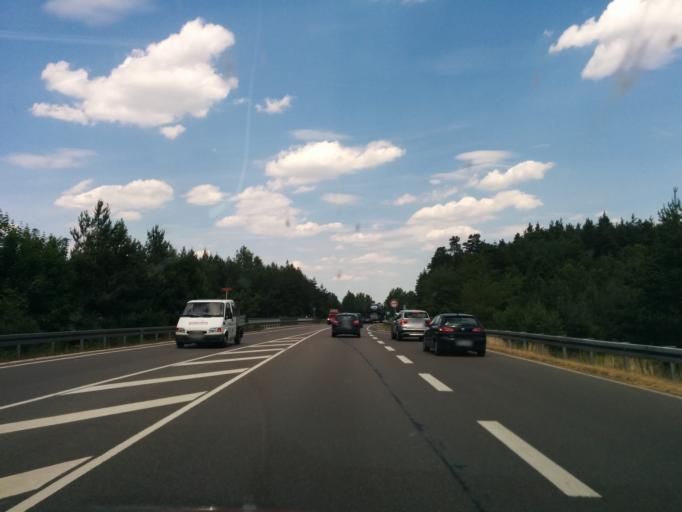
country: DE
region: Bavaria
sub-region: Regierungsbezirk Mittelfranken
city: Pleinfeld
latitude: 49.1099
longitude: 10.9996
